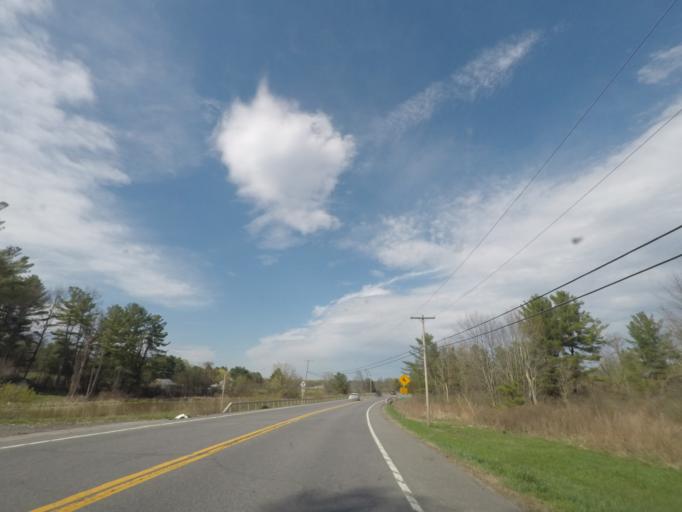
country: US
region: New York
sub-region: Albany County
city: Voorheesville
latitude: 42.5452
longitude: -73.9410
